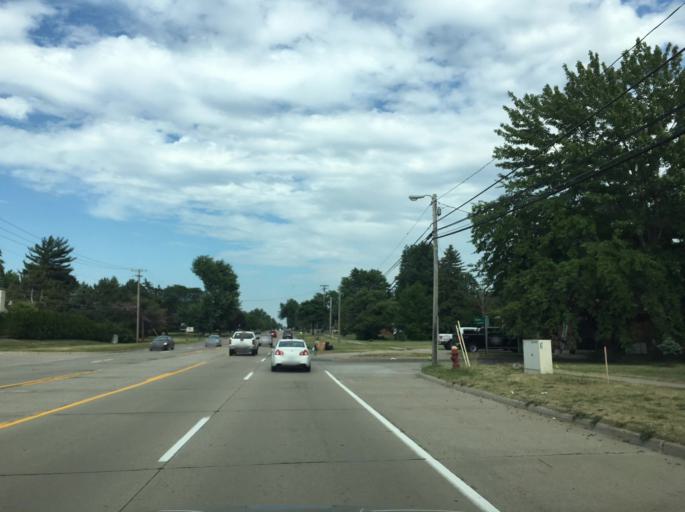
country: US
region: Michigan
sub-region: Macomb County
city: Sterling Heights
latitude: 42.5357
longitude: -83.0606
